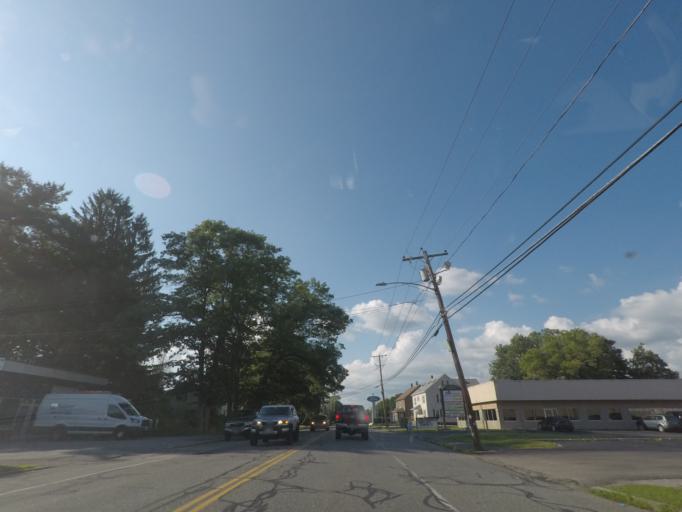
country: US
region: Massachusetts
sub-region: Worcester County
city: Webster
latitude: 42.0572
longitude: -71.8631
